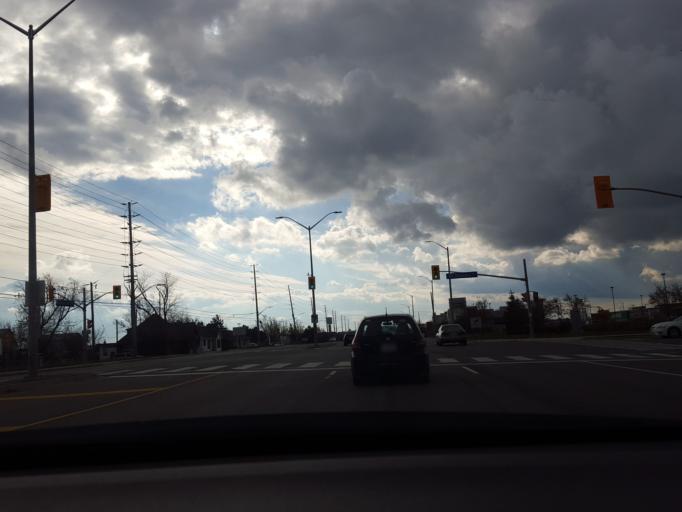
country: CA
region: Ontario
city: Brampton
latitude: 43.6396
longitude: -79.7136
